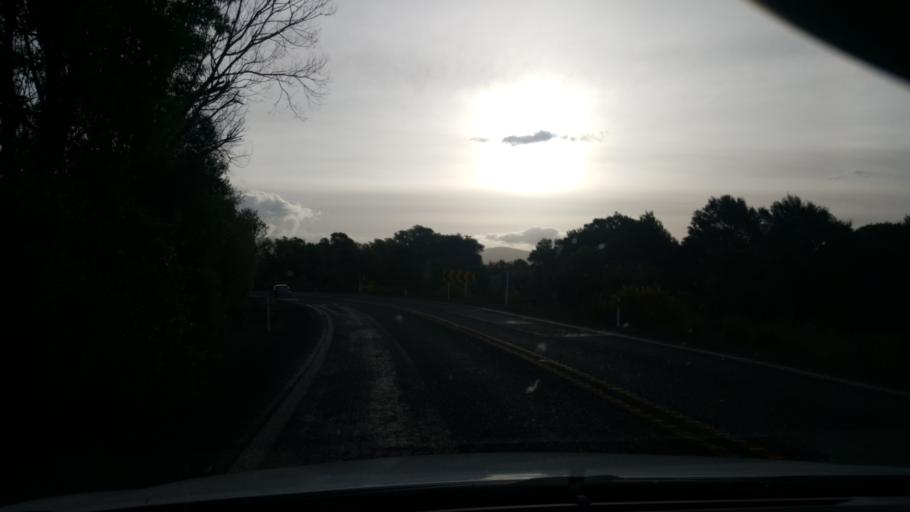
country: NZ
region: Waikato
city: Turangi
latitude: -38.9443
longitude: 175.8528
